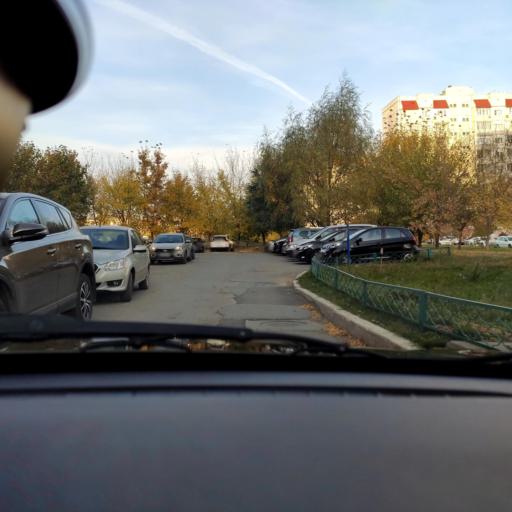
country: RU
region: Samara
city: Tol'yatti
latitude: 53.5483
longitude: 49.3249
